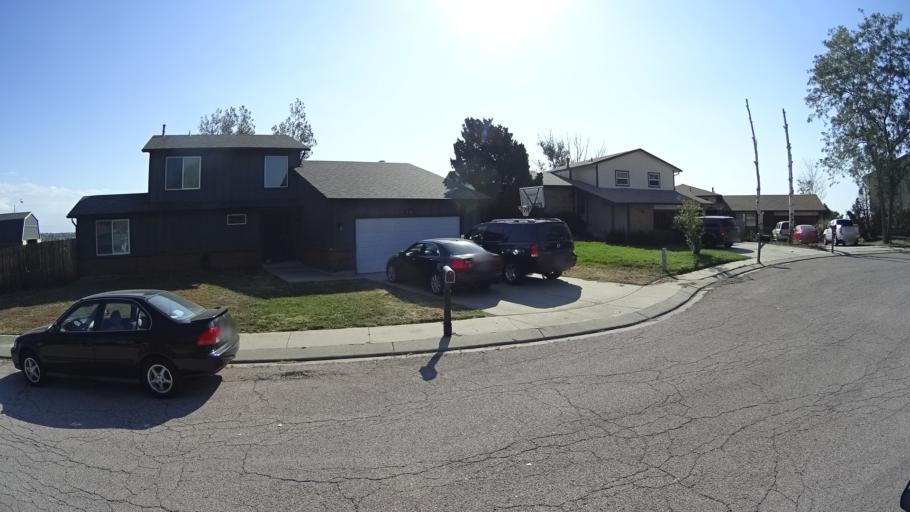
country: US
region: Colorado
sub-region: El Paso County
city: Cimarron Hills
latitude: 38.8869
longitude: -104.7230
